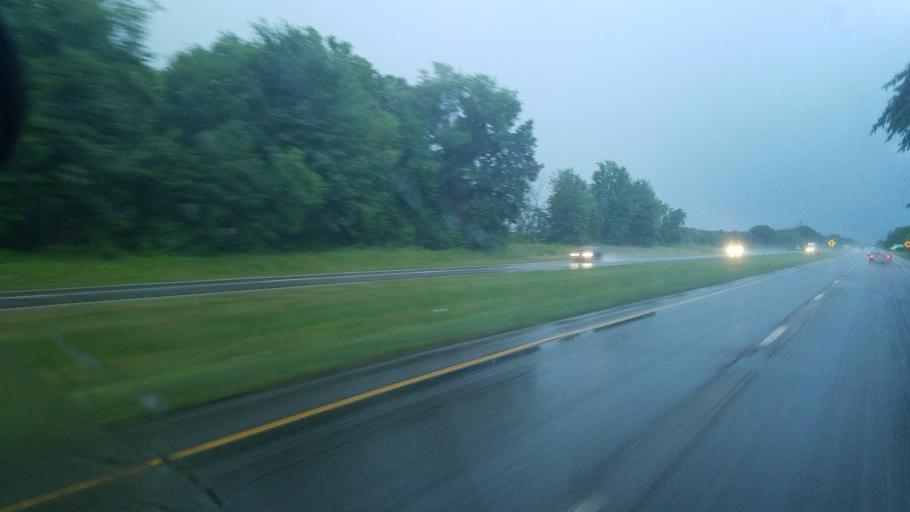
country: US
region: Ohio
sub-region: Wayne County
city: Doylestown
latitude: 40.9757
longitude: -81.6621
